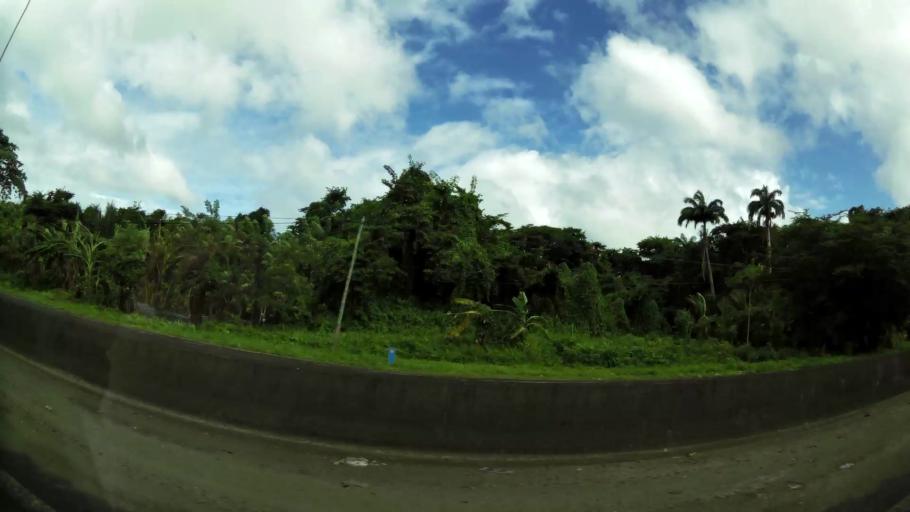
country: GP
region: Guadeloupe
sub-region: Guadeloupe
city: Pointe-a-Pitre
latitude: 16.2541
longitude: -61.5393
